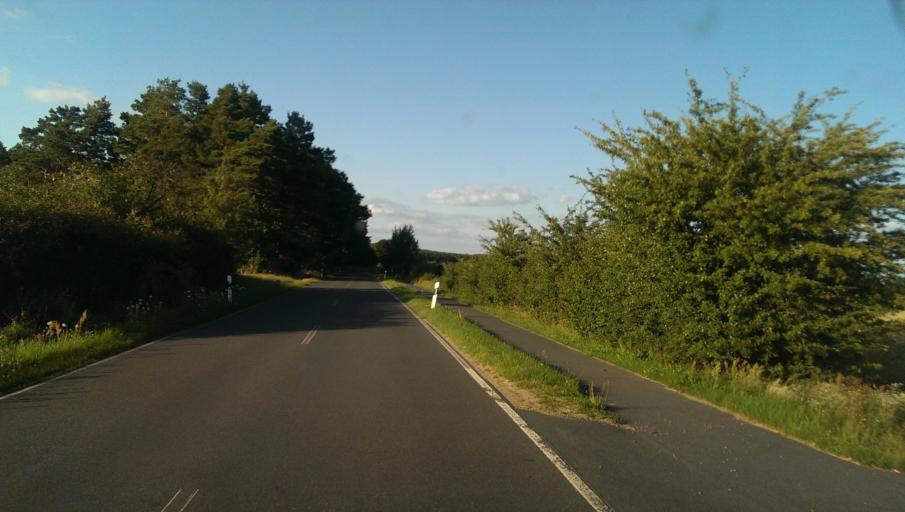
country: DE
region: Brandenburg
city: Luckenwalde
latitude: 52.1846
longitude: 13.1249
